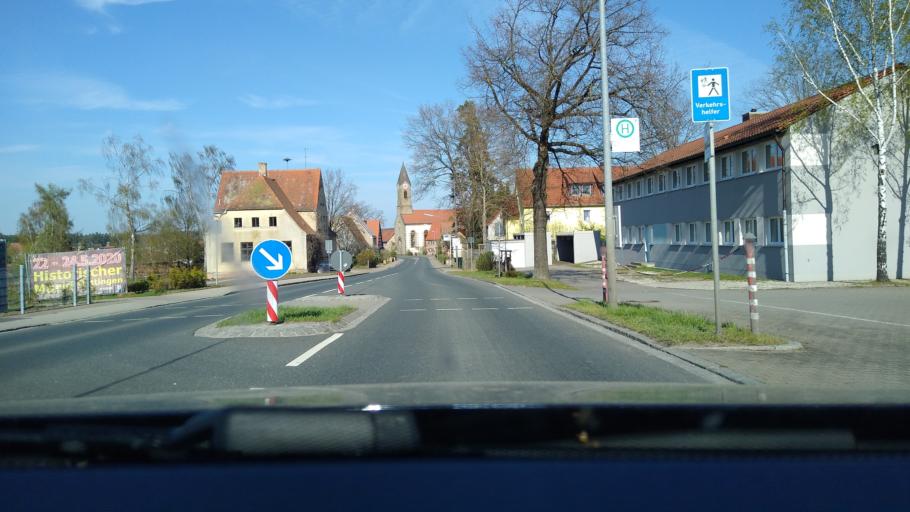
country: DE
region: Bavaria
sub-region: Regierungsbezirk Mittelfranken
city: Spalt
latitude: 49.2152
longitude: 10.8804
